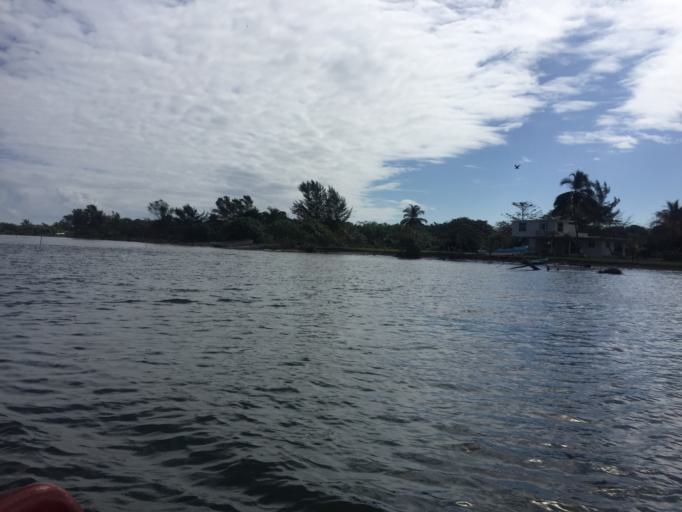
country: MX
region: Veracruz
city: Tecolutla
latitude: 20.4701
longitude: -97.0071
